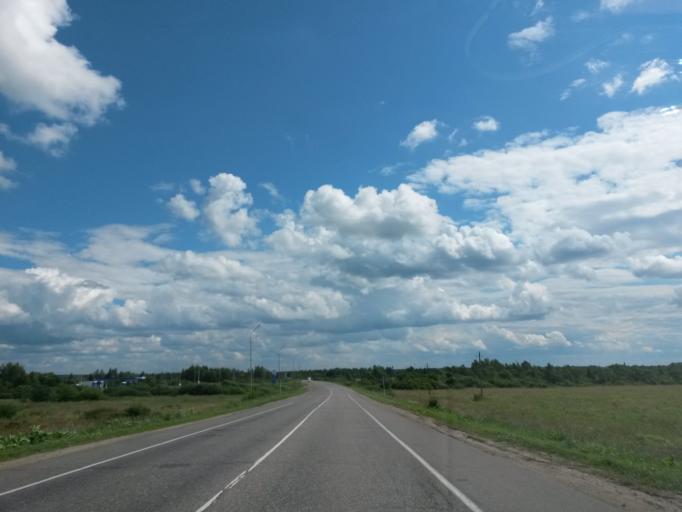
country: RU
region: Ivanovo
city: Pistsovo
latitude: 57.1709
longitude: 40.5135
